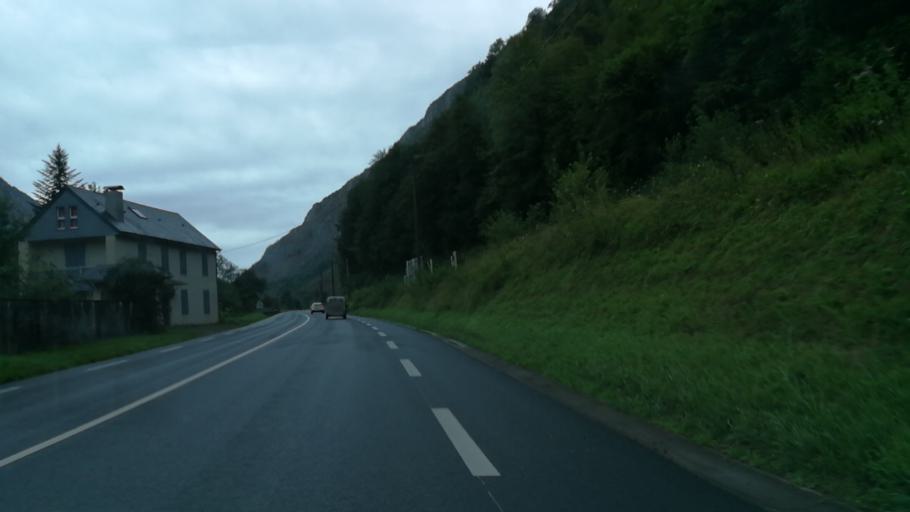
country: FR
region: Aquitaine
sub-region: Departement des Pyrenees-Atlantiques
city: Arette
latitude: 43.0566
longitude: -0.5967
